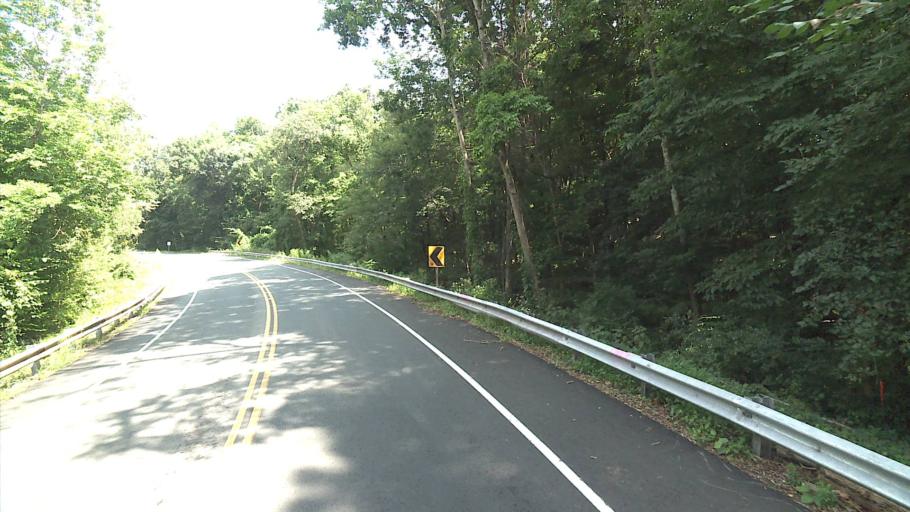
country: US
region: Connecticut
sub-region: Hartford County
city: Broad Brook
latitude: 41.9122
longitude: -72.5583
